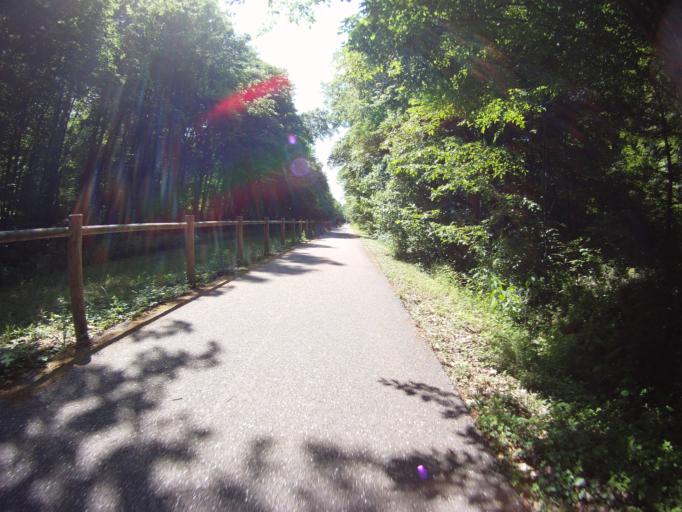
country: FR
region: Lorraine
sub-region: Departement de Meurthe-et-Moselle
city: Champenoux
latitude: 48.7513
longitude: 6.3245
